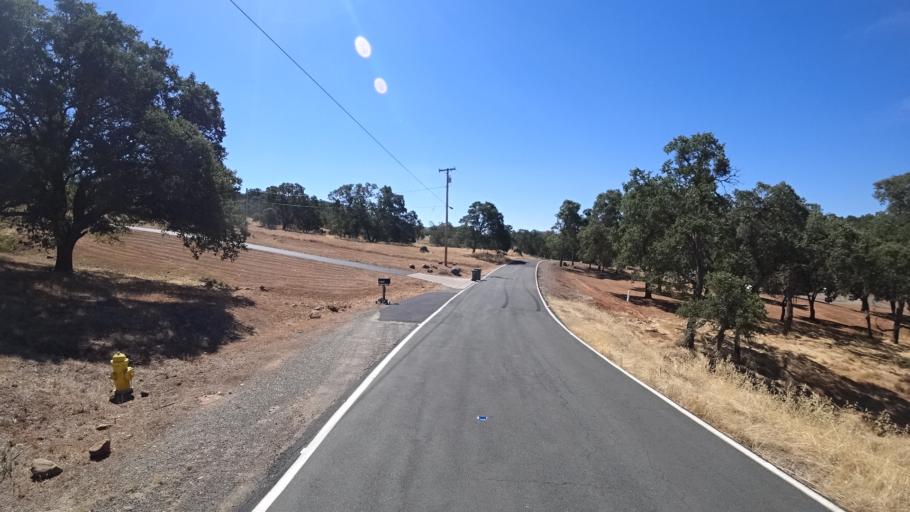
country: US
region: California
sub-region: Calaveras County
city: Rancho Calaveras
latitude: 38.1399
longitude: -120.8509
